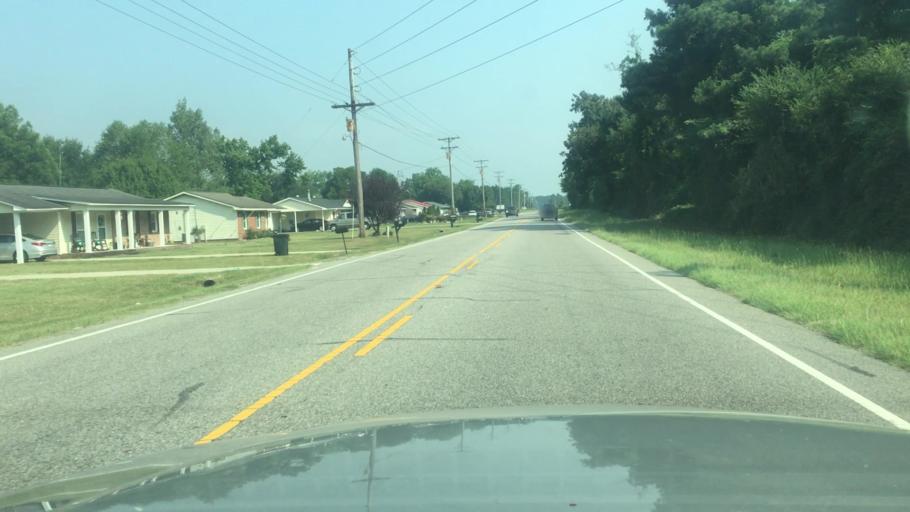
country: US
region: North Carolina
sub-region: Cumberland County
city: Hope Mills
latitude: 34.8988
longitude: -78.9000
